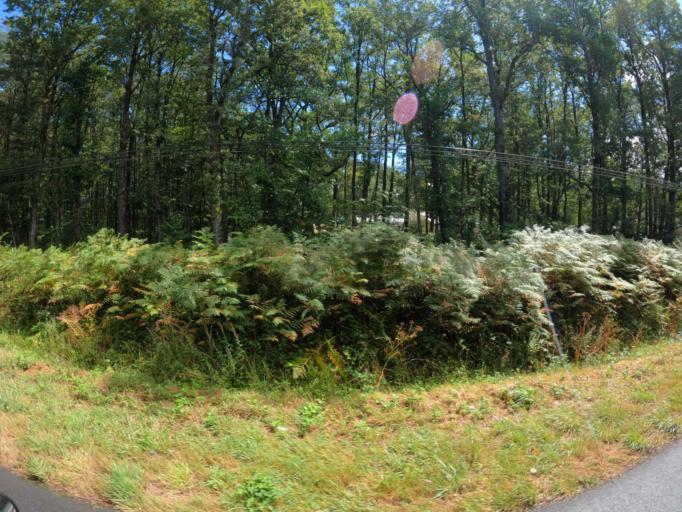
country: FR
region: Pays de la Loire
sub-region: Departement de Maine-et-Loire
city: Feneu
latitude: 47.5821
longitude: -0.5915
